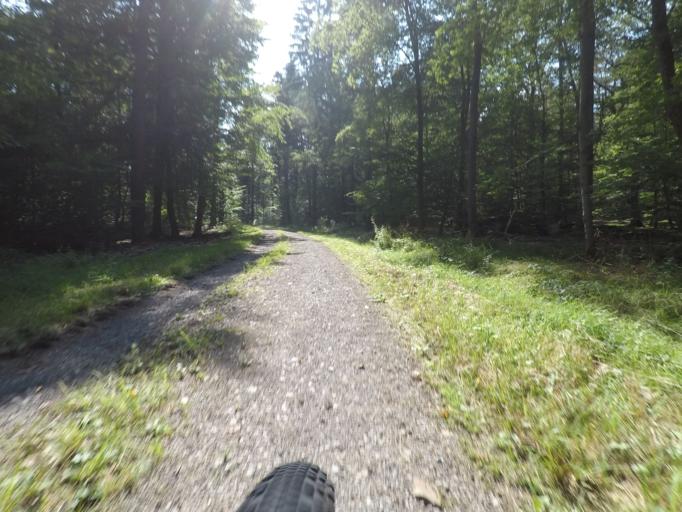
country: DE
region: Baden-Wuerttemberg
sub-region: Regierungsbezirk Stuttgart
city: Steinenbronn
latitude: 48.6820
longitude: 9.1031
